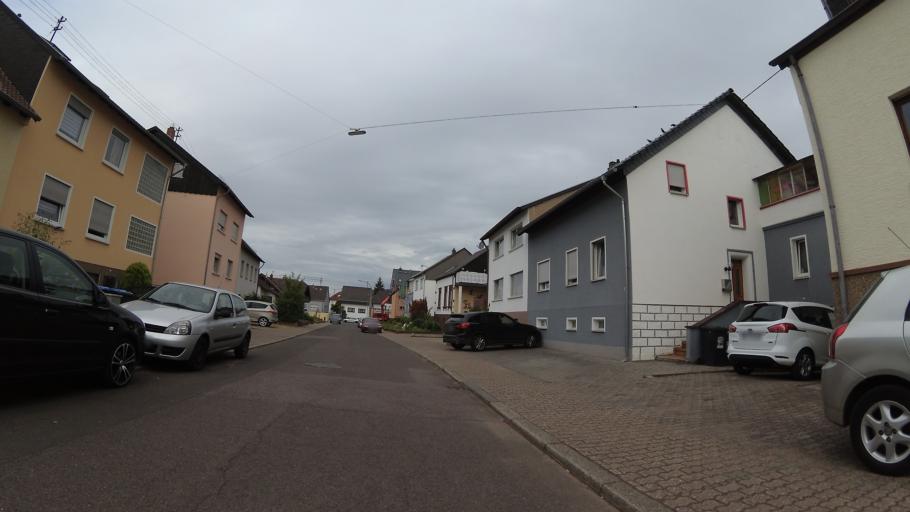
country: DE
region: Saarland
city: Schwalbach
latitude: 49.3148
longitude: 6.8117
